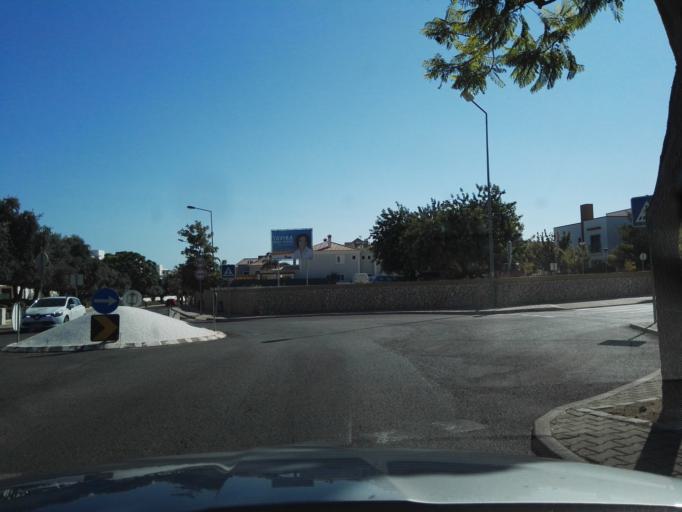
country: PT
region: Faro
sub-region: Tavira
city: Tavira
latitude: 37.1181
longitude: -7.6511
